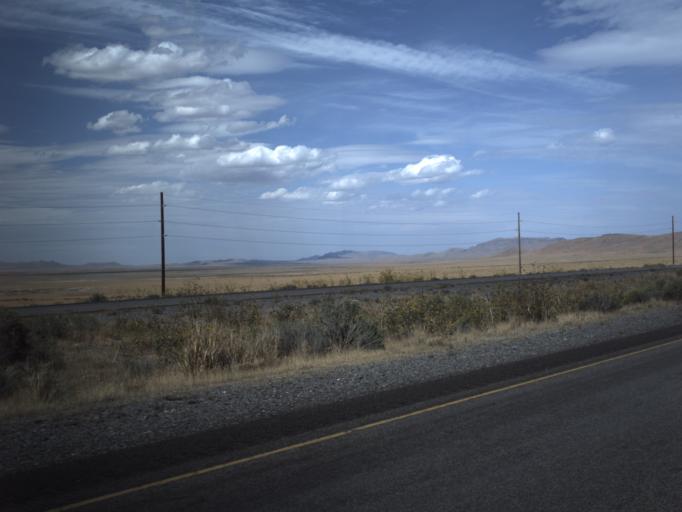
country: US
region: Utah
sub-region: Tooele County
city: Grantsville
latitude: 40.8055
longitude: -112.9360
